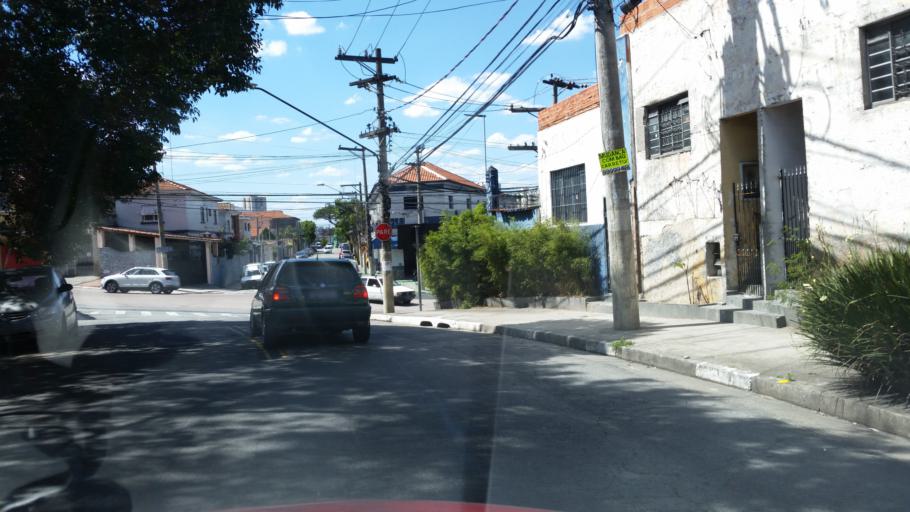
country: BR
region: Sao Paulo
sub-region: Diadema
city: Diadema
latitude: -23.6230
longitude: -46.6295
